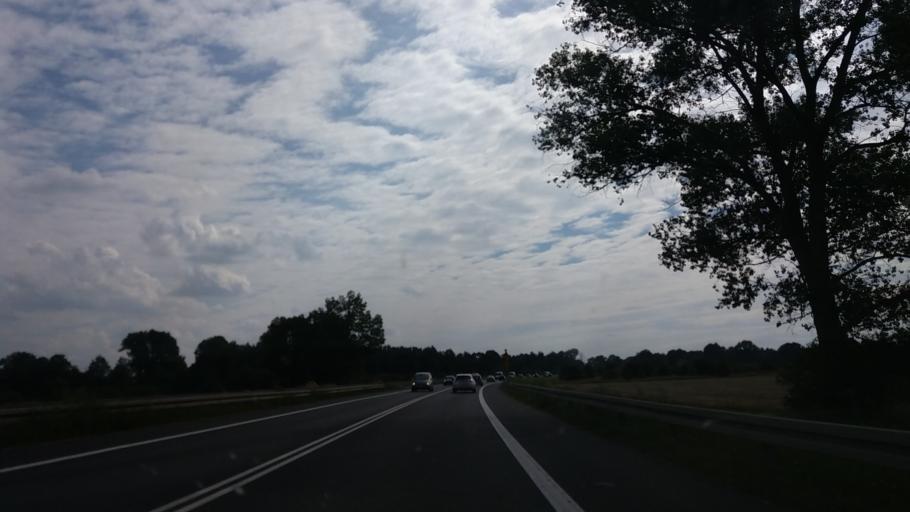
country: PL
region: Lubusz
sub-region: Powiat zielonogorski
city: Sulechow
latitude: 52.0204
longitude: 15.6291
